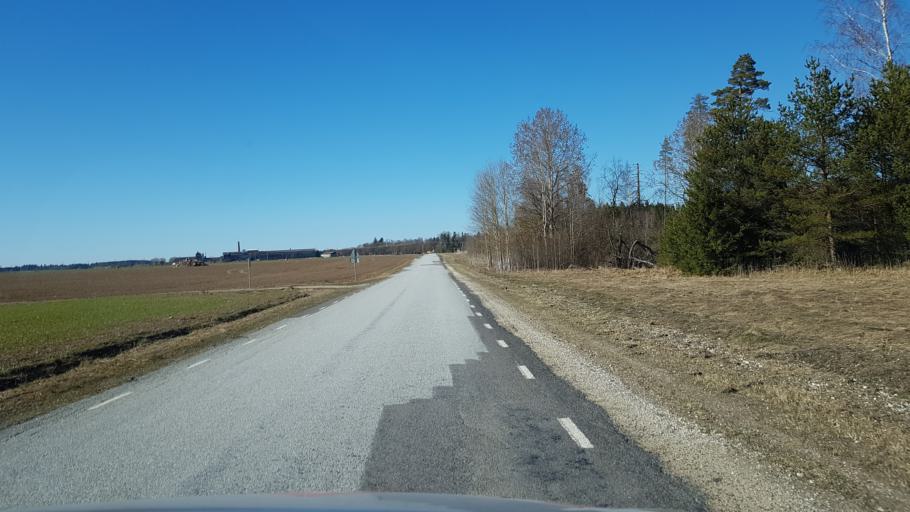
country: EE
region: Laeaene-Virumaa
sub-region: Viru-Nigula vald
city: Kunda
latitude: 59.3835
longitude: 26.5743
